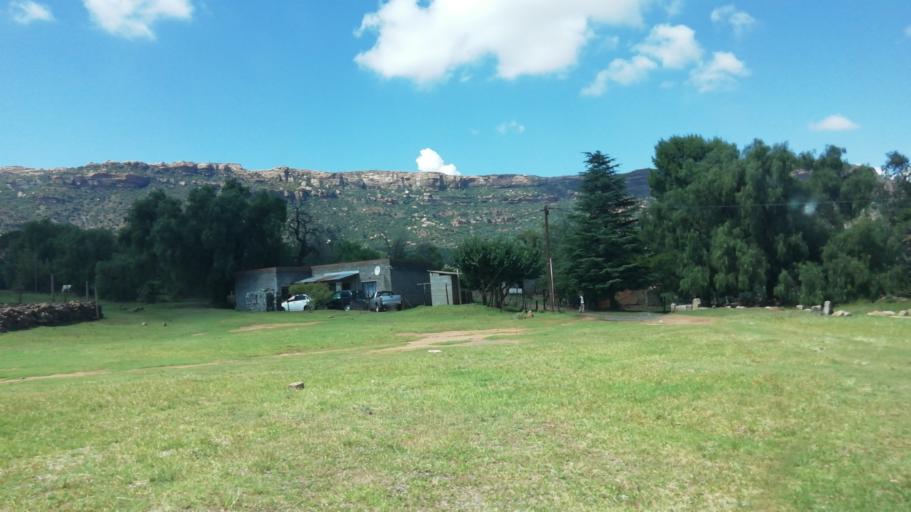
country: LS
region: Maseru
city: Nako
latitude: -29.6243
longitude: 27.5129
